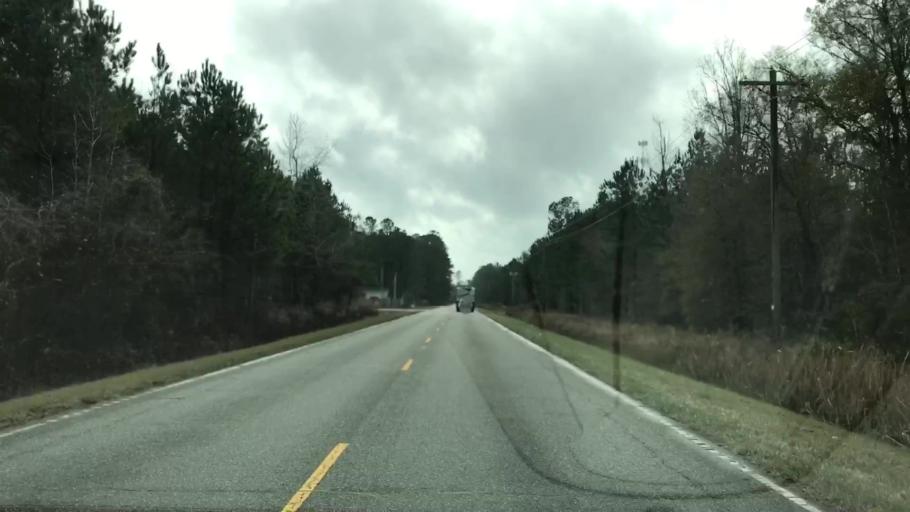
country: US
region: South Carolina
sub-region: Georgetown County
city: Murrells Inlet
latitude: 33.6263
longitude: -79.1905
